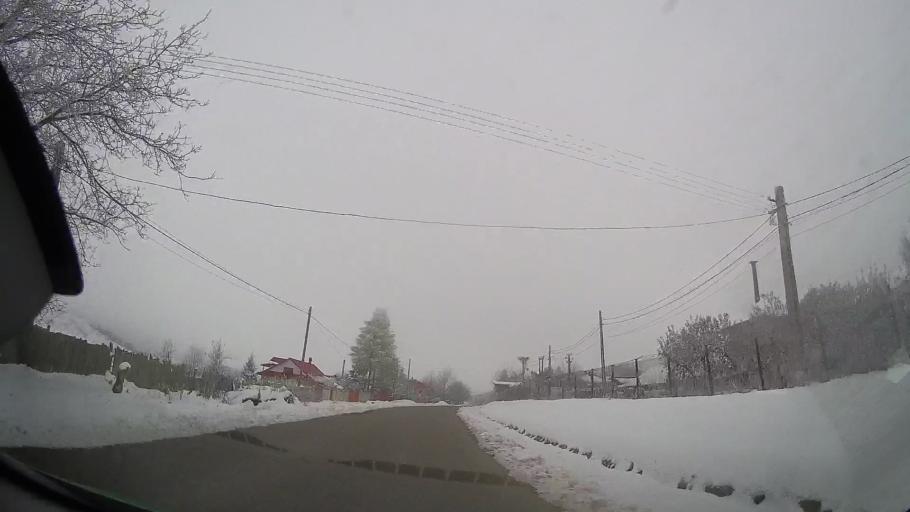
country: RO
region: Neamt
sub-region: Comuna Icusesti
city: Balusesti
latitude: 46.8573
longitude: 27.0255
